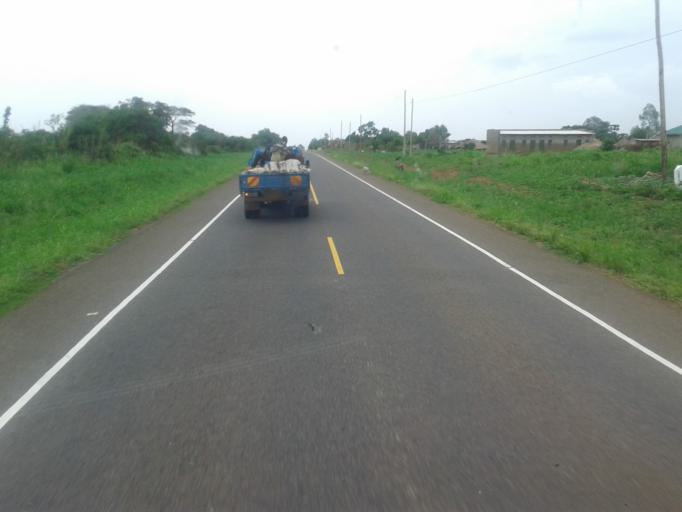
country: UG
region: Northern Region
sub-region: Oyam District
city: Oyam
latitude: 2.1432
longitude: 32.2088
